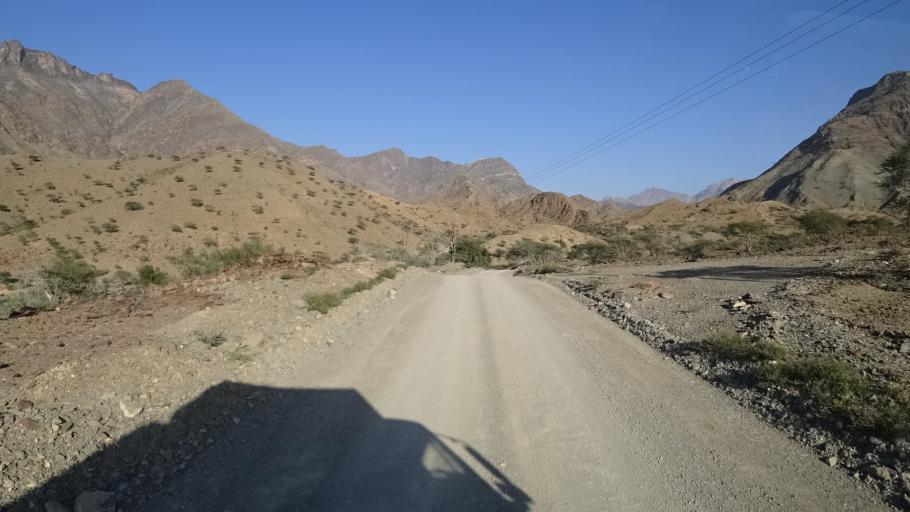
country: OM
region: Al Batinah
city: Rustaq
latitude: 23.2755
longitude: 57.3652
